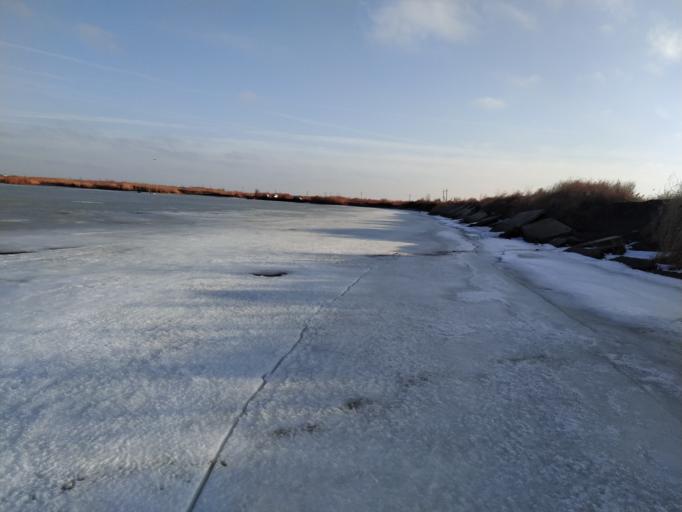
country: RU
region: Rostov
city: Bataysk
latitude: 47.1449
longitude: 39.6589
